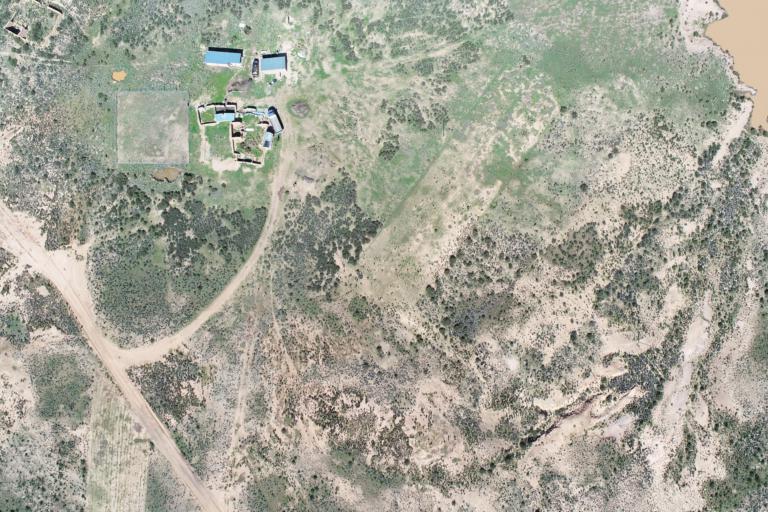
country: BO
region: La Paz
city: Curahuara de Carangas
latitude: -17.2941
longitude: -68.5123
